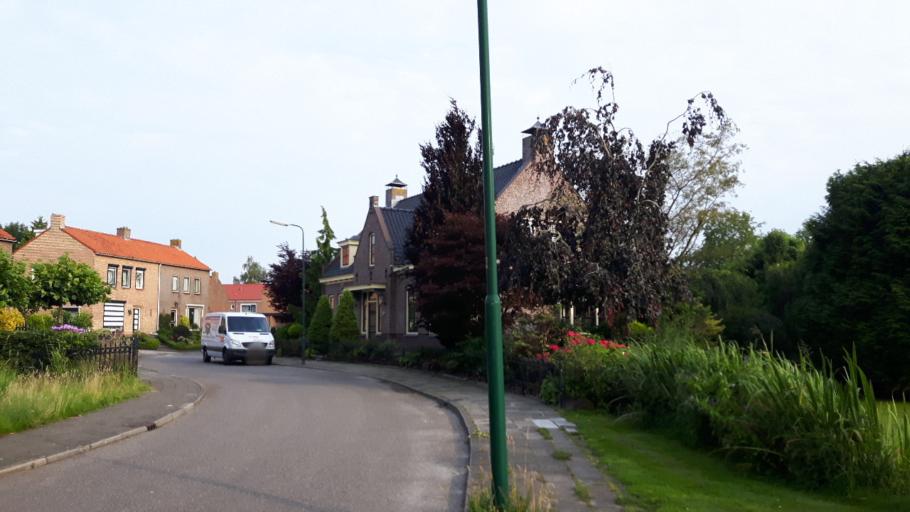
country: NL
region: Utrecht
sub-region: Gemeente Woerden
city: Woerden
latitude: 52.1110
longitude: 4.8955
